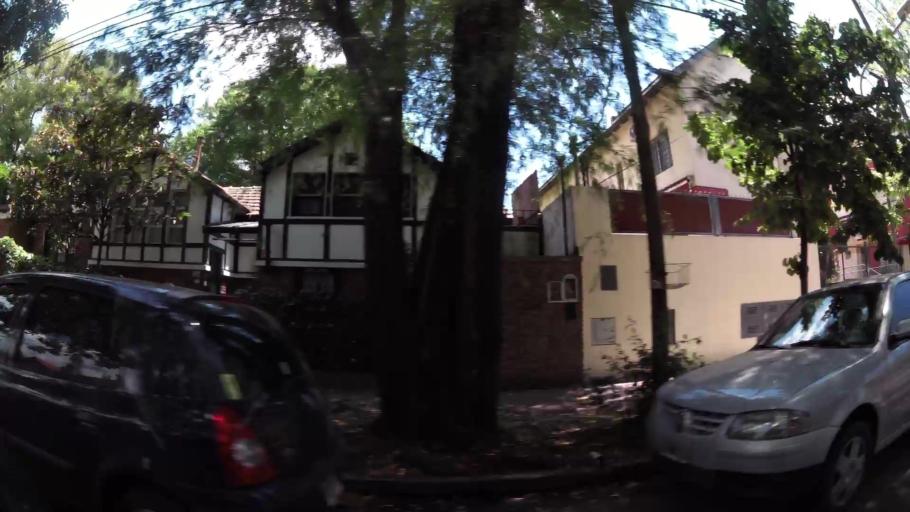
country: AR
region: Buenos Aires
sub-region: Partido de Tigre
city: Tigre
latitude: -34.4196
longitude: -58.5824
